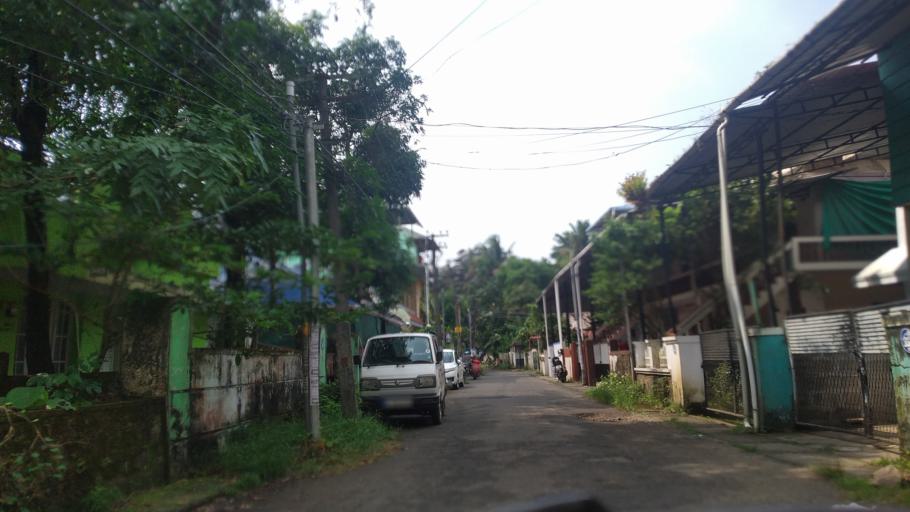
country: IN
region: Kerala
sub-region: Ernakulam
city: Cochin
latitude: 9.9785
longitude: 76.3049
